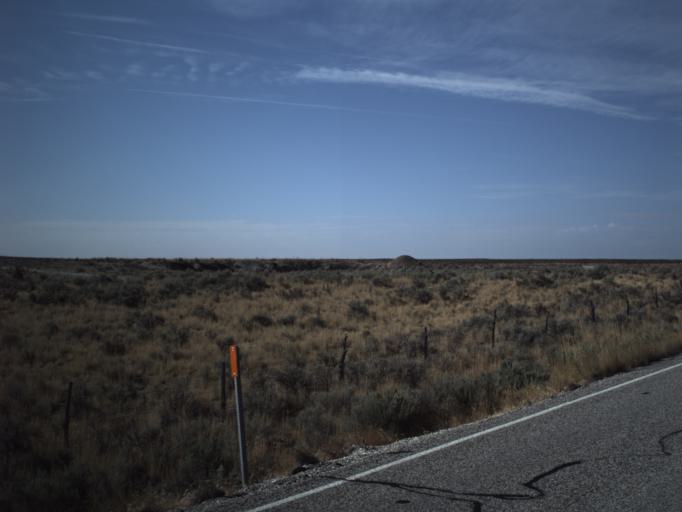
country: US
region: Idaho
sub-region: Minidoka County
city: Rupert
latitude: 41.8314
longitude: -113.1600
